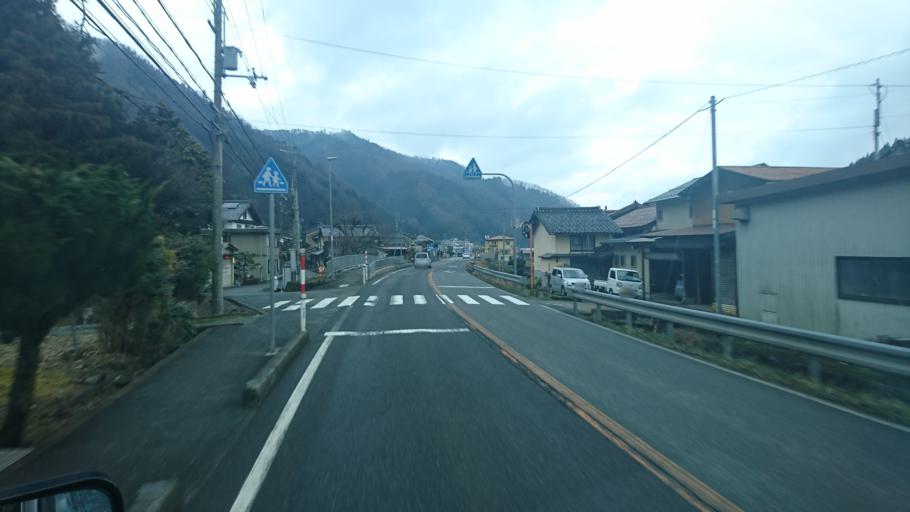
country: JP
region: Hyogo
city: Toyooka
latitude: 35.3869
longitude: 134.6832
